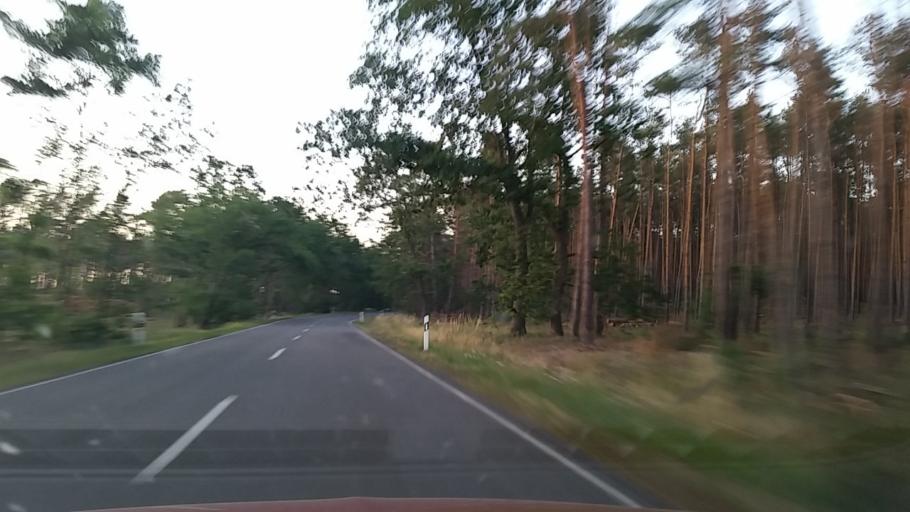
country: DE
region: Saxony-Anhalt
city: Jessen
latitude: 51.7721
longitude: 12.9513
